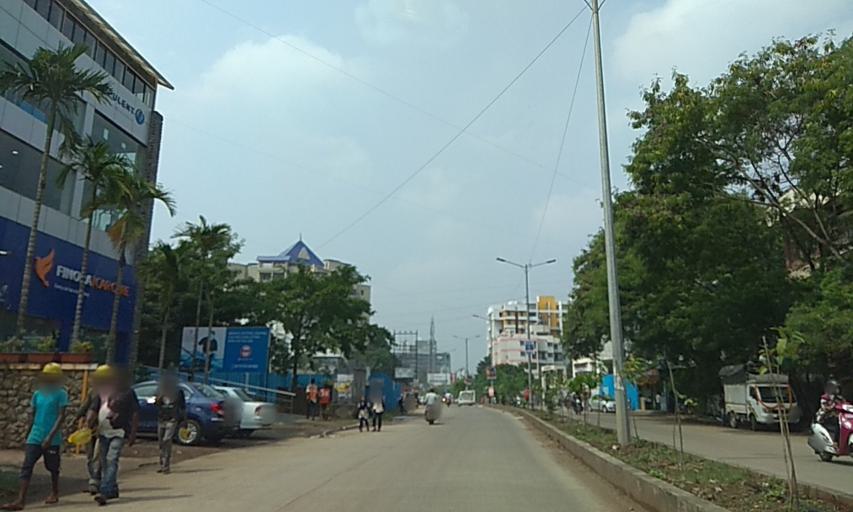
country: IN
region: Maharashtra
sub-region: Pune Division
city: Pimpri
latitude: 18.5585
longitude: 73.7759
